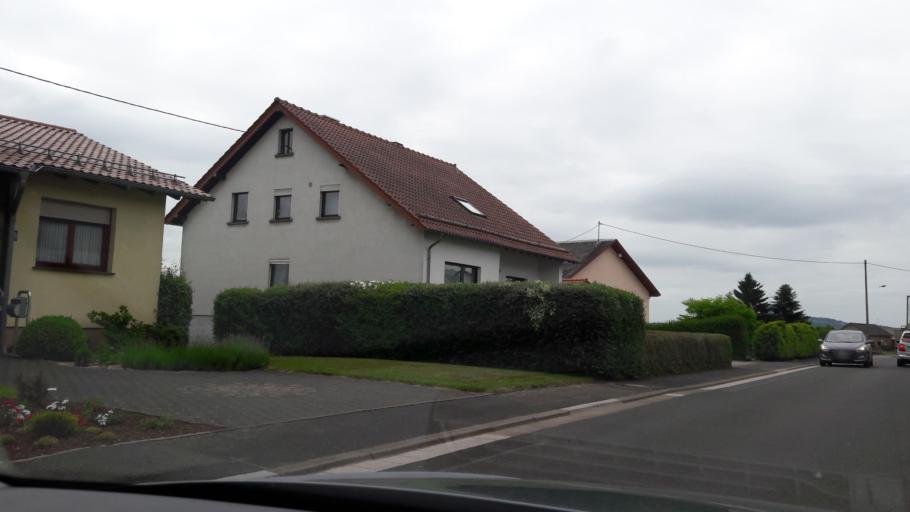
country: DE
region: Saarland
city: Tholey
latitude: 49.5332
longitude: 7.0337
